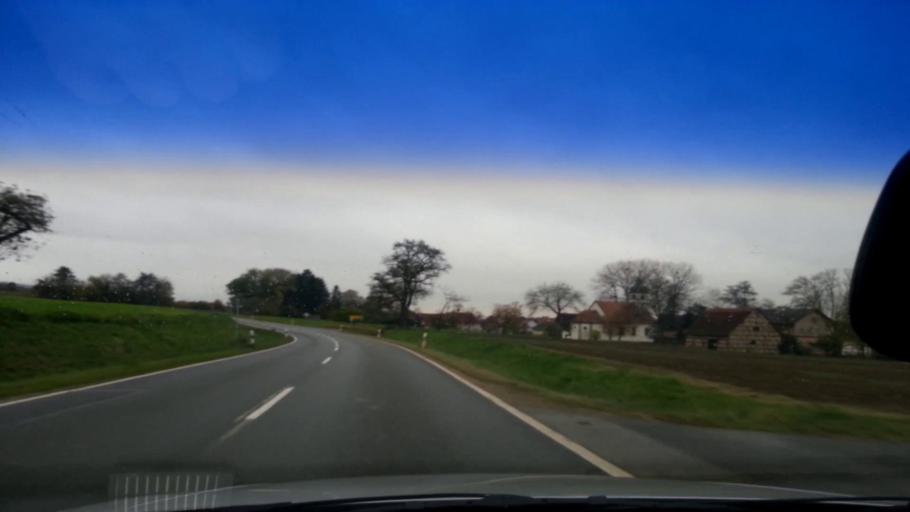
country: DE
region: Bavaria
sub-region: Upper Franconia
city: Schesslitz
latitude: 50.0006
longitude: 11.0607
